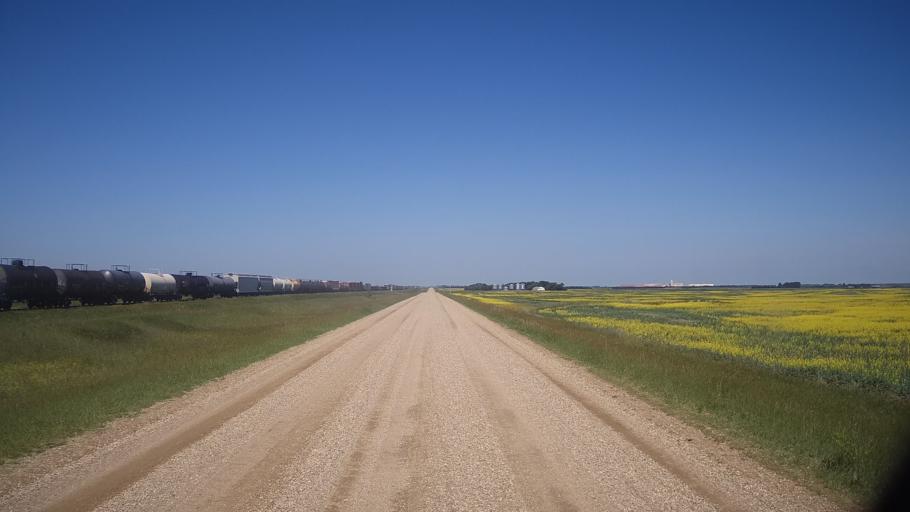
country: CA
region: Saskatchewan
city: Watrous
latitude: 51.8591
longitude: -105.9591
